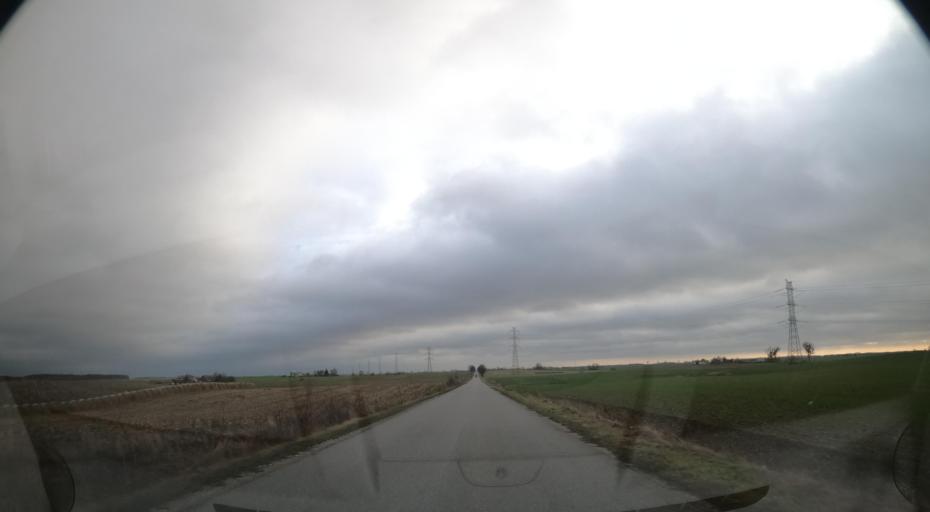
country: PL
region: Kujawsko-Pomorskie
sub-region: Powiat nakielski
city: Sadki
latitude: 53.1812
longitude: 17.4065
